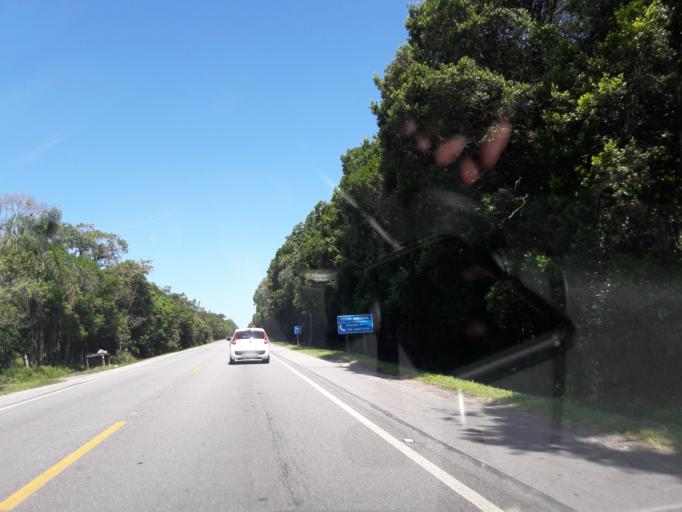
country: BR
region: Parana
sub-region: Pontal Do Parana
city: Pontal do Parana
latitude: -25.6236
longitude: -48.5438
